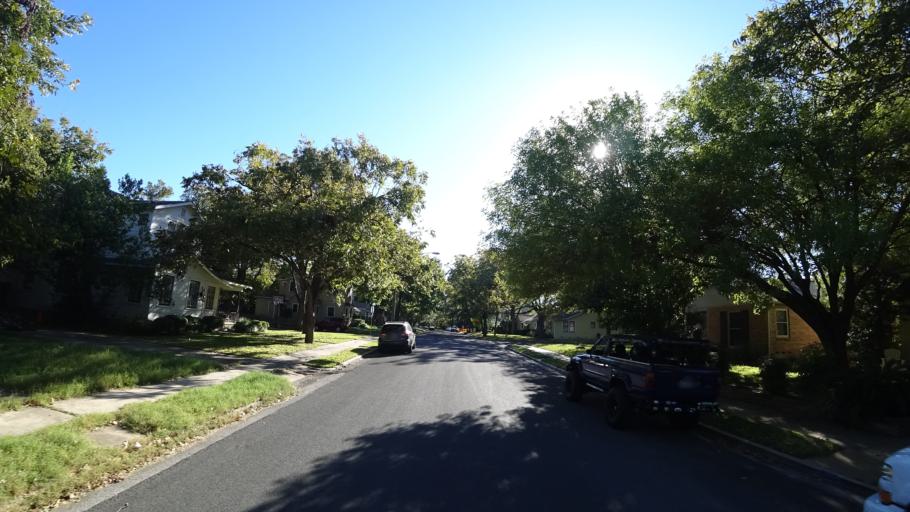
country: US
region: Texas
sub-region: Travis County
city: Austin
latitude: 30.3053
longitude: -97.7525
